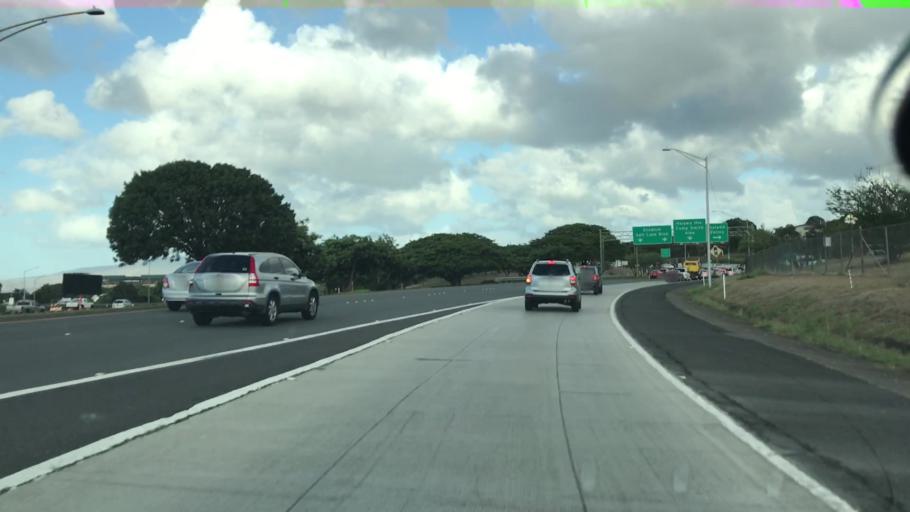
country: US
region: Hawaii
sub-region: Honolulu County
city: Halawa Heights
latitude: 21.3715
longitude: -157.9159
